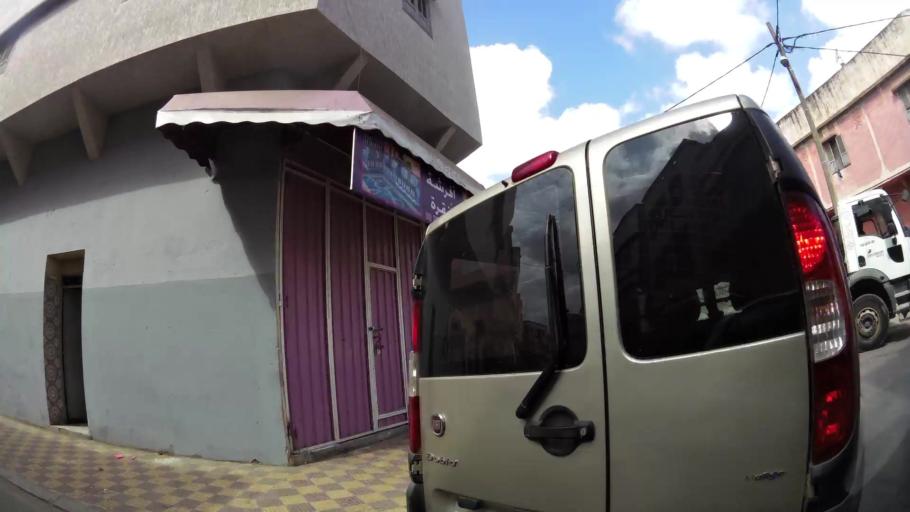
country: MA
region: Gharb-Chrarda-Beni Hssen
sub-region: Kenitra Province
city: Kenitra
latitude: 34.2615
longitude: -6.5666
